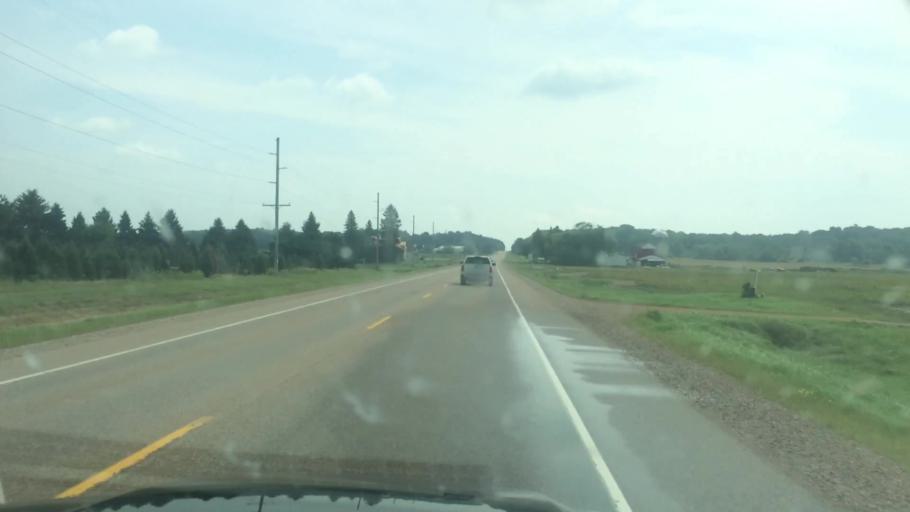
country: US
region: Wisconsin
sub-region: Langlade County
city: Antigo
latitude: 45.1619
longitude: -89.0774
